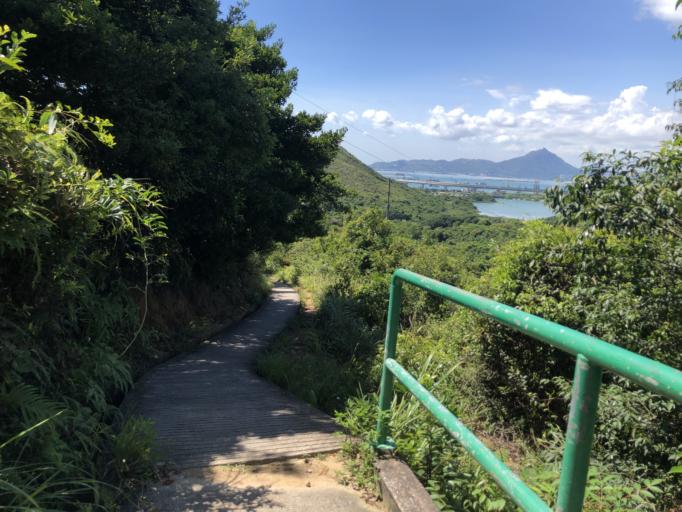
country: HK
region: Tuen Mun
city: Tuen Mun
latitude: 22.2878
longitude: 113.9813
